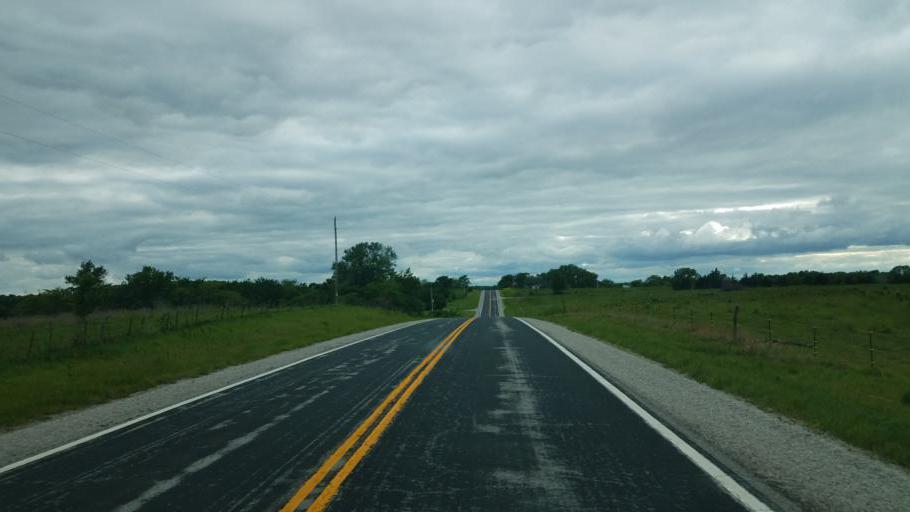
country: US
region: Missouri
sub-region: Mercer County
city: Princeton
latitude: 40.3741
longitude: -93.7141
